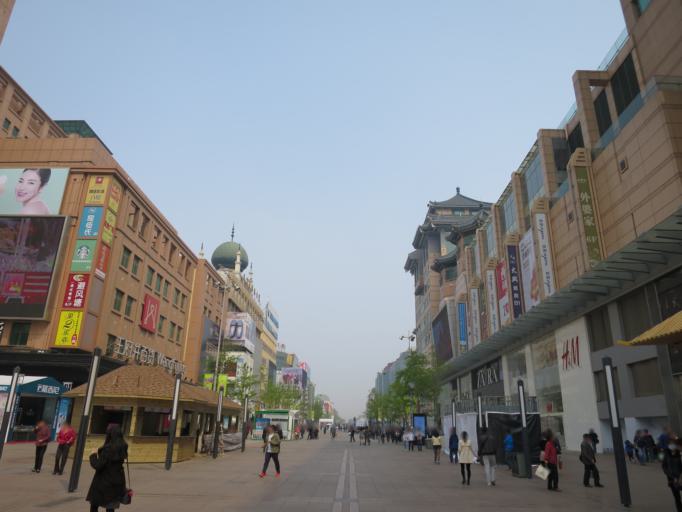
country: CN
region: Beijing
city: Beijing
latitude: 39.9120
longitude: 116.4052
